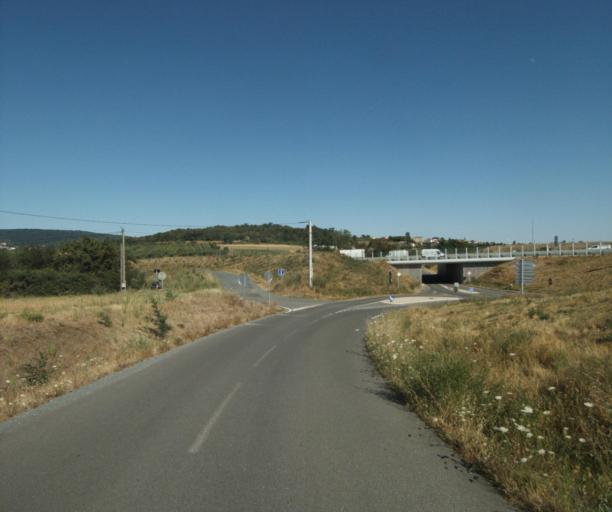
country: FR
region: Rhone-Alpes
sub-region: Departement du Rhone
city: La Tour-de-Salvagny
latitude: 45.8262
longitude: 4.7367
